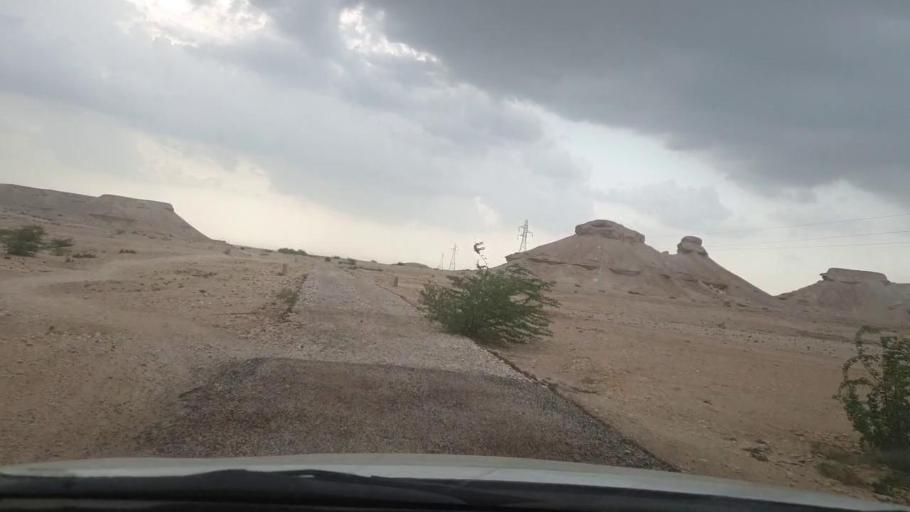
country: PK
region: Sindh
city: Khairpur
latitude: 27.4707
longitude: 68.8929
